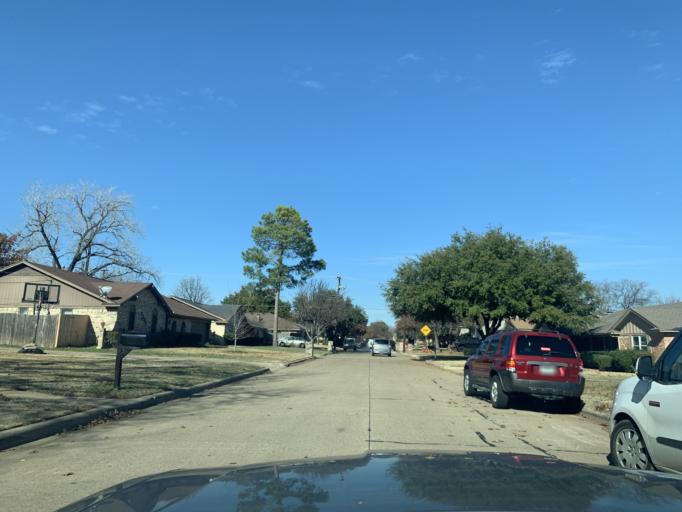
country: US
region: Texas
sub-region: Tarrant County
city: Bedford
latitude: 32.8421
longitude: -97.1535
